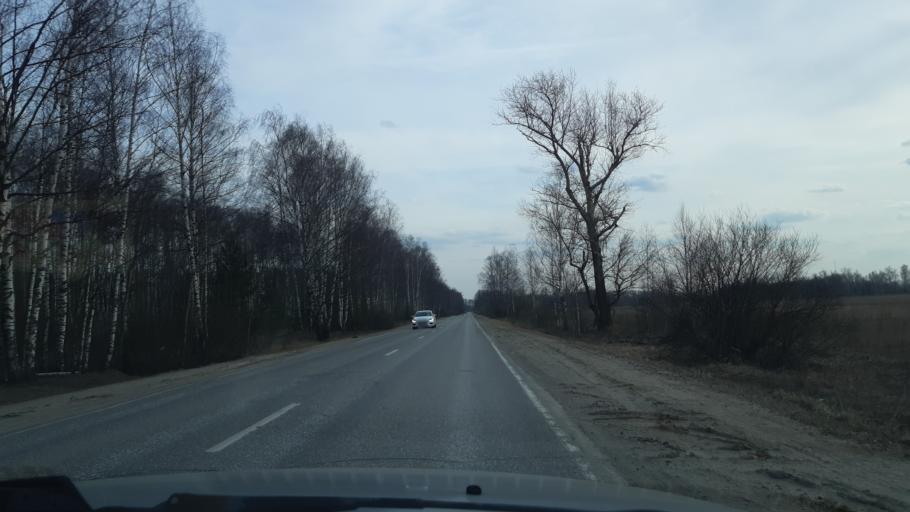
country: RU
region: Vladimir
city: Luknovo
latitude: 56.2339
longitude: 42.0343
